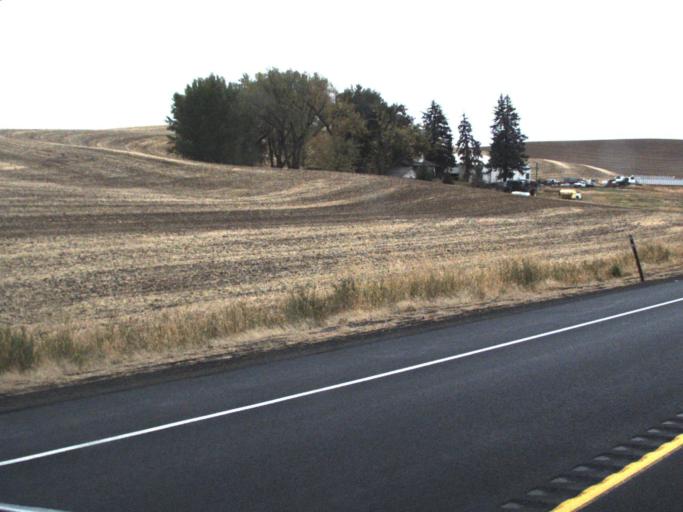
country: US
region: Washington
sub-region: Whitman County
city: Pullman
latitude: 46.7621
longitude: -117.2647
